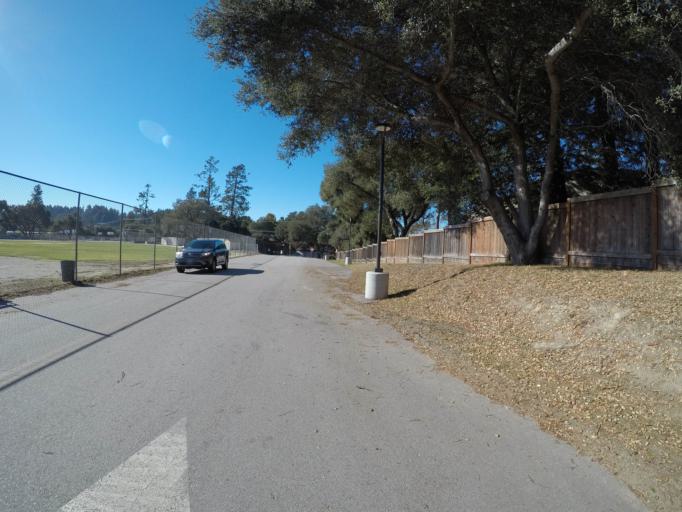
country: US
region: California
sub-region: Santa Cruz County
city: Scotts Valley
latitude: 37.0471
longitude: -122.0236
